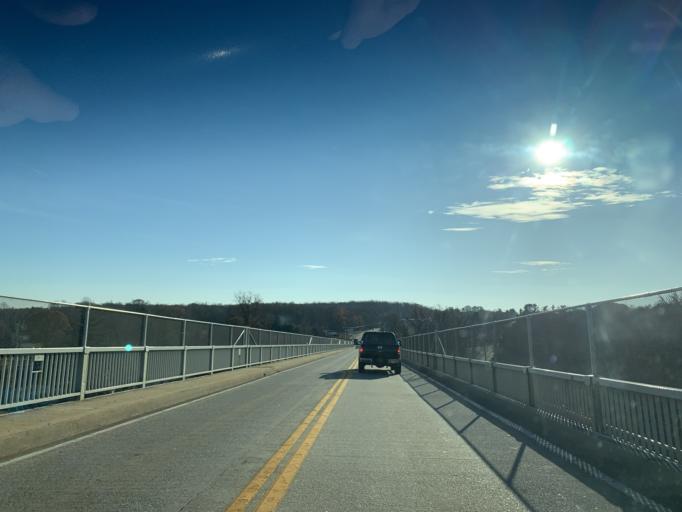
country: US
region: Maryland
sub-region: Cecil County
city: Elkton
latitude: 39.5253
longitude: -75.8157
